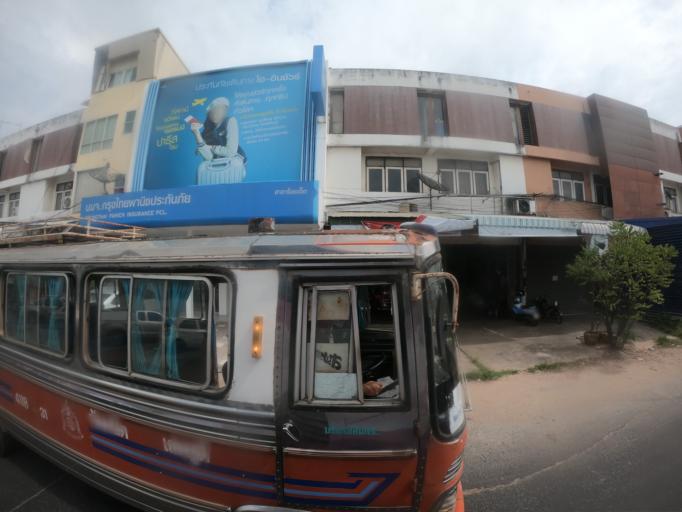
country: TH
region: Roi Et
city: Roi Et
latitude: 16.0544
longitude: 103.6402
